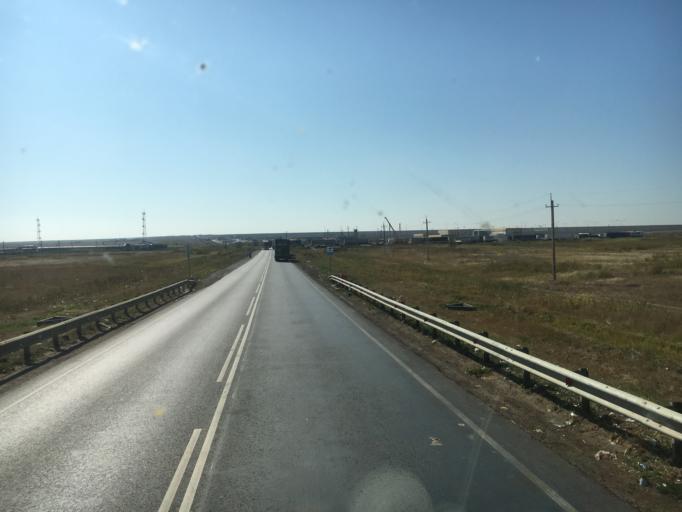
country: KZ
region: Batys Qazaqstan
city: Peremetnoe
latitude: 51.6836
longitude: 51.0031
